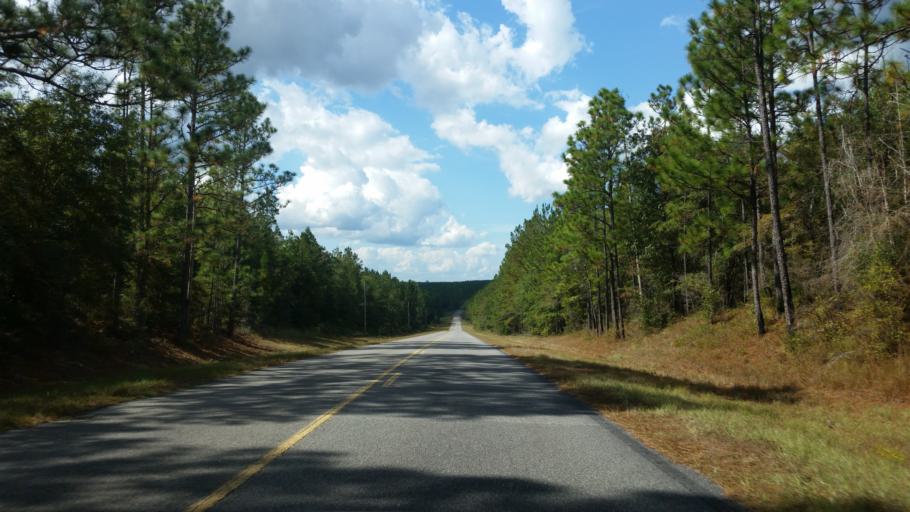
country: US
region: Alabama
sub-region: Escambia County
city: Atmore
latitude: 30.8878
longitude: -87.5339
